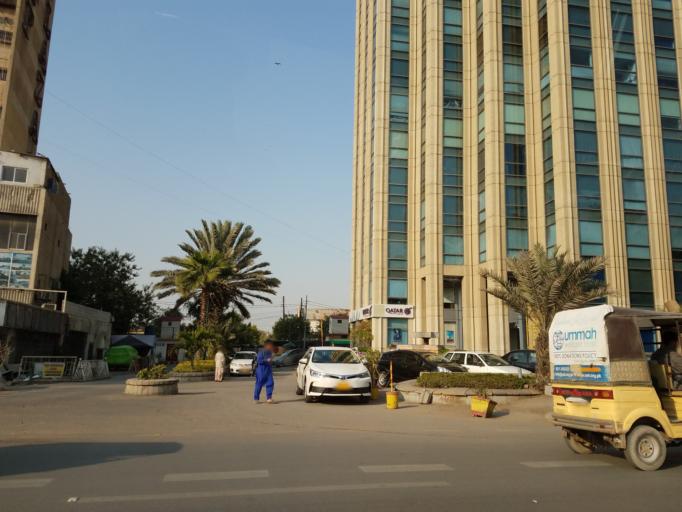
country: PK
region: Sindh
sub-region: Karachi District
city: Karachi
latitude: 24.8573
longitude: 67.0445
